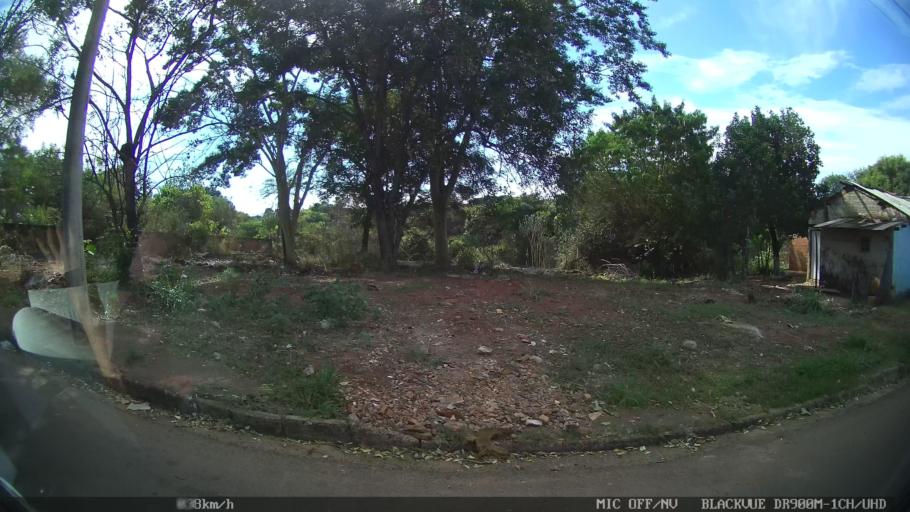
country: BR
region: Sao Paulo
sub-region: Sao Jose Do Rio Preto
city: Sao Jose do Rio Preto
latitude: -20.8433
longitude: -49.3373
